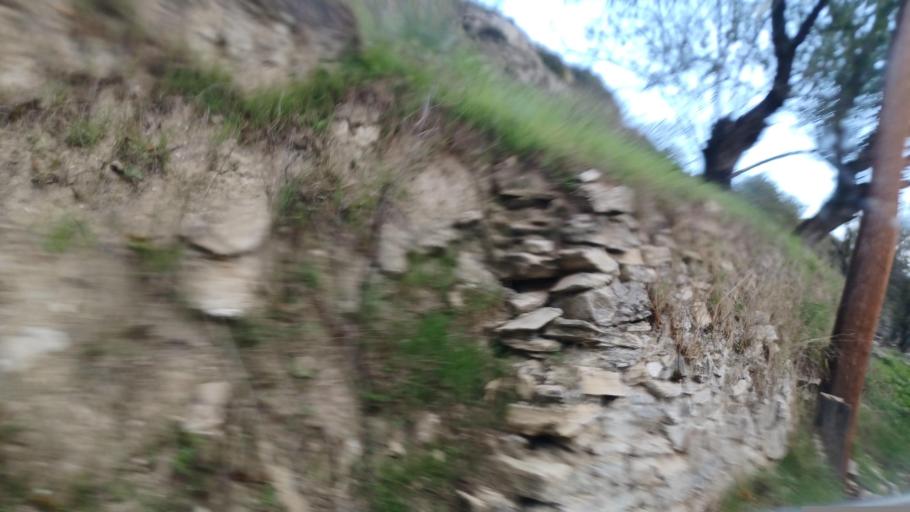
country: CY
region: Pafos
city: Mesogi
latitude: 34.8546
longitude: 32.5188
